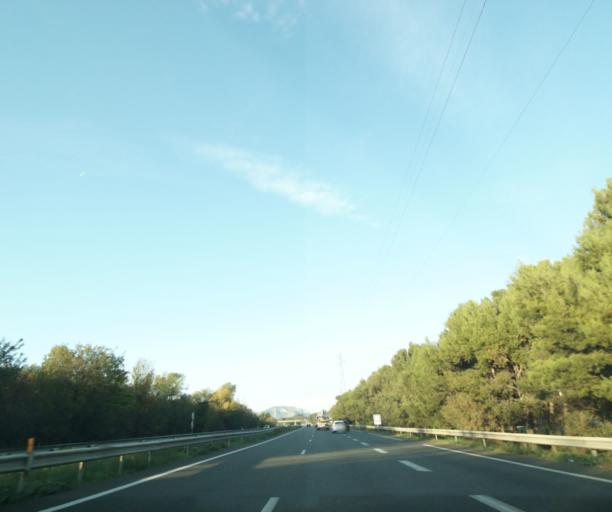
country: FR
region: Provence-Alpes-Cote d'Azur
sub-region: Departement des Bouches-du-Rhone
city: Aubagne
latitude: 43.3016
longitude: 5.5910
